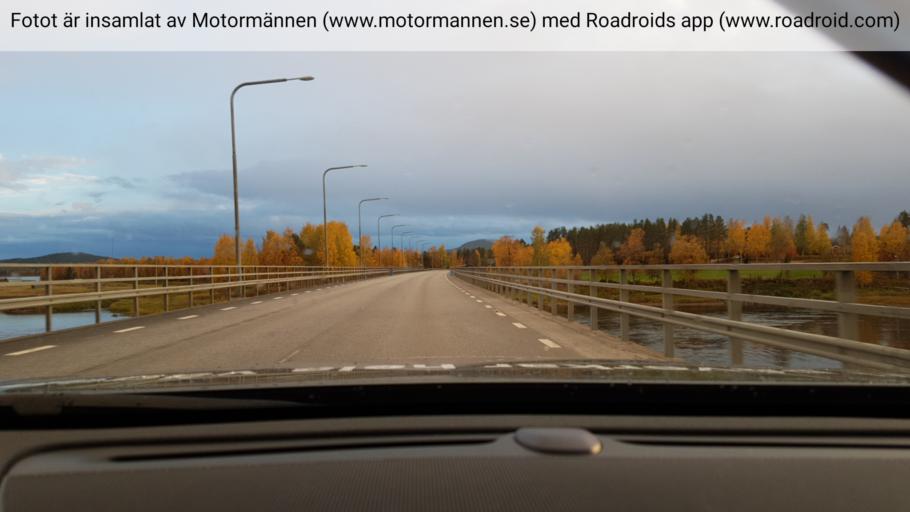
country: SE
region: Norrbotten
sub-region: Overkalix Kommun
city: OEverkalix
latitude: 66.3646
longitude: 22.8414
